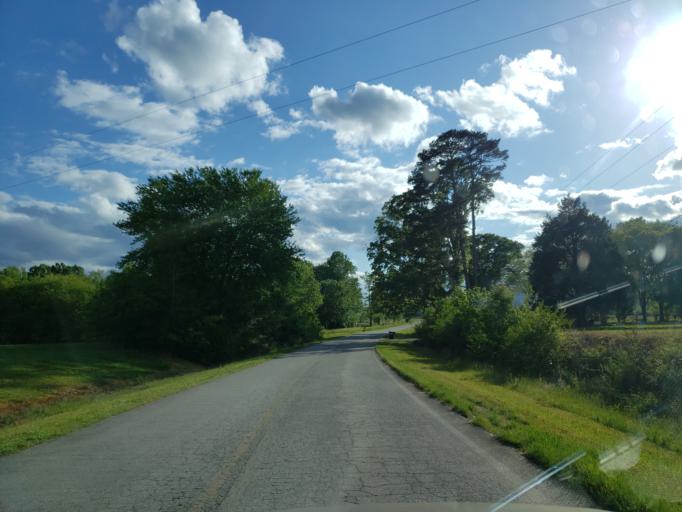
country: US
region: Georgia
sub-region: Haralson County
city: Tallapoosa
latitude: 33.7872
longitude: -85.2976
